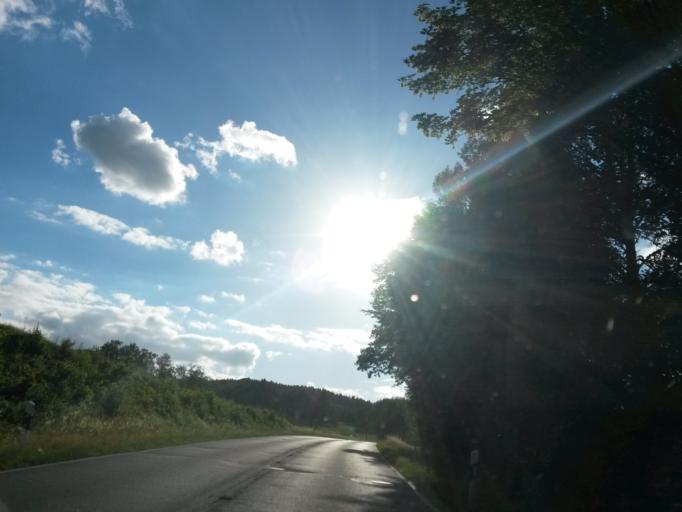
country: DE
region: North Rhine-Westphalia
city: Bergneustadt
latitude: 51.0468
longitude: 7.6897
